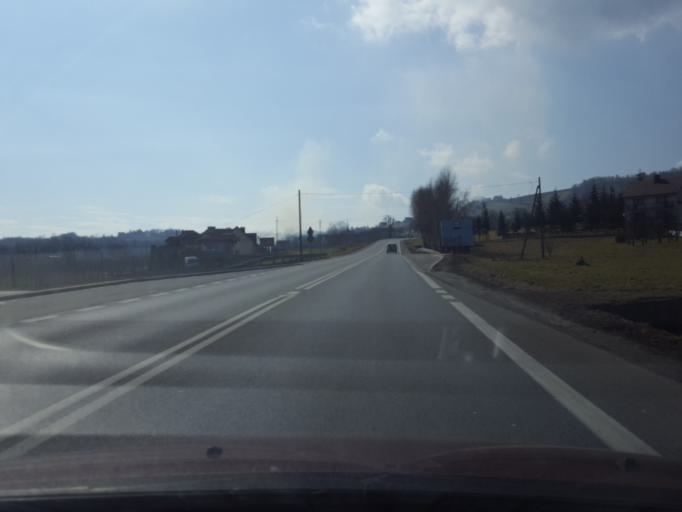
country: PL
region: Lesser Poland Voivodeship
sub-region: Powiat nowosadecki
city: Lososina Dolna
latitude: 49.7372
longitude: 20.6376
